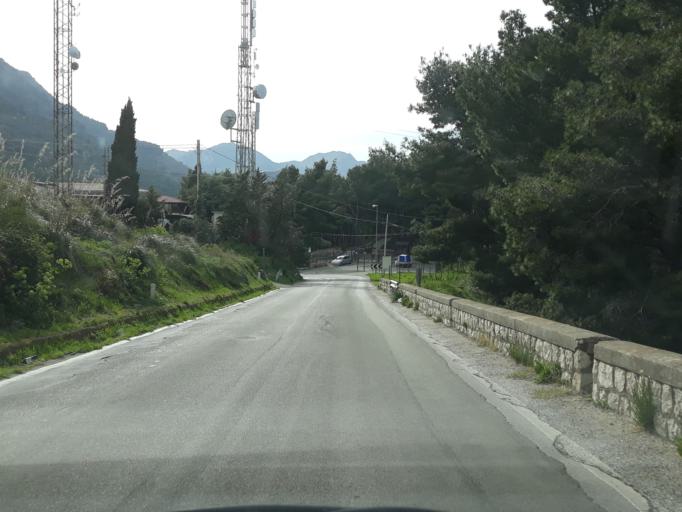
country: IT
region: Sicily
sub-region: Palermo
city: Altofonte
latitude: 38.0442
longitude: 13.3053
